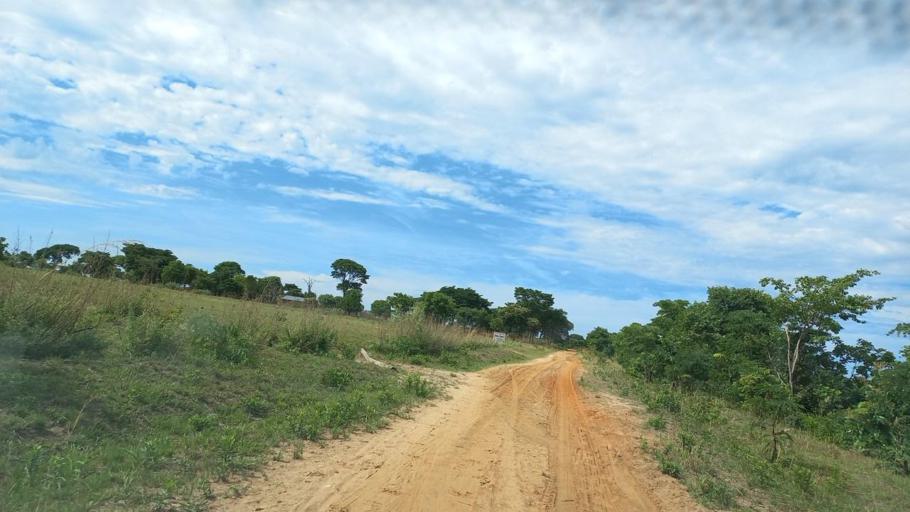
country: ZM
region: North-Western
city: Kabompo
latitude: -13.5123
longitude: 24.3923
